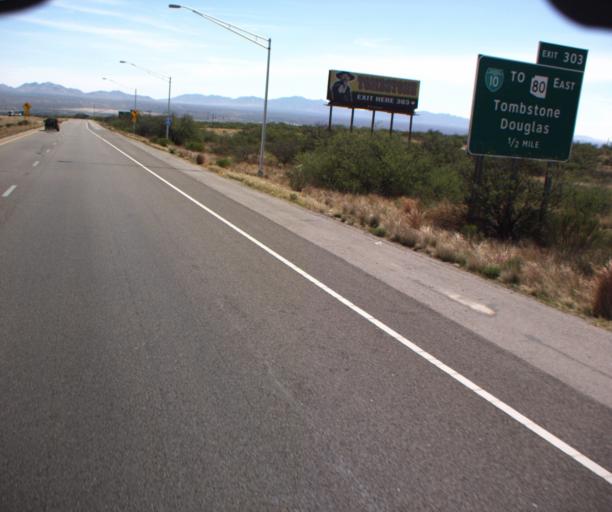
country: US
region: Arizona
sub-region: Cochise County
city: Whetstone
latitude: 31.9664
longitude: -110.3387
